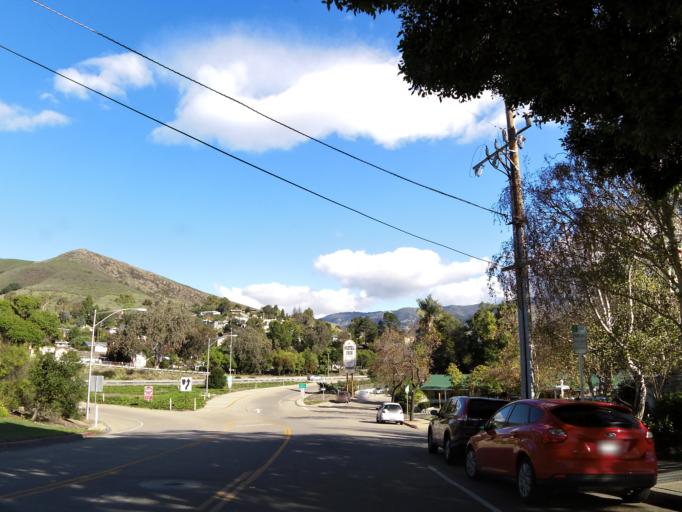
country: US
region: California
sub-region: San Luis Obispo County
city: San Luis Obispo
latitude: 35.2907
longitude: -120.6493
